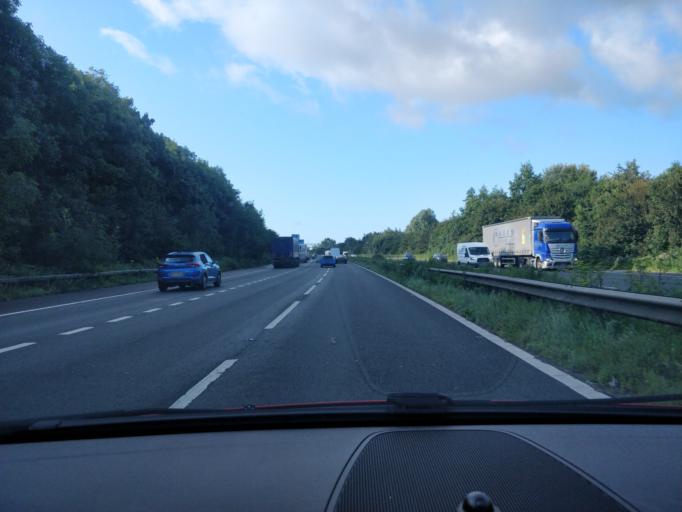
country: GB
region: England
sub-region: Knowsley
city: Prescot
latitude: 53.4109
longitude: -2.8136
